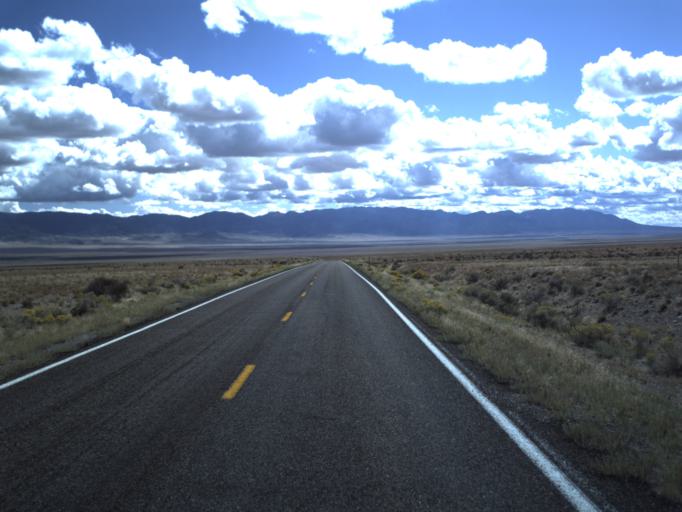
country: US
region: Utah
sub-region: Beaver County
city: Milford
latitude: 38.5879
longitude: -113.8165
